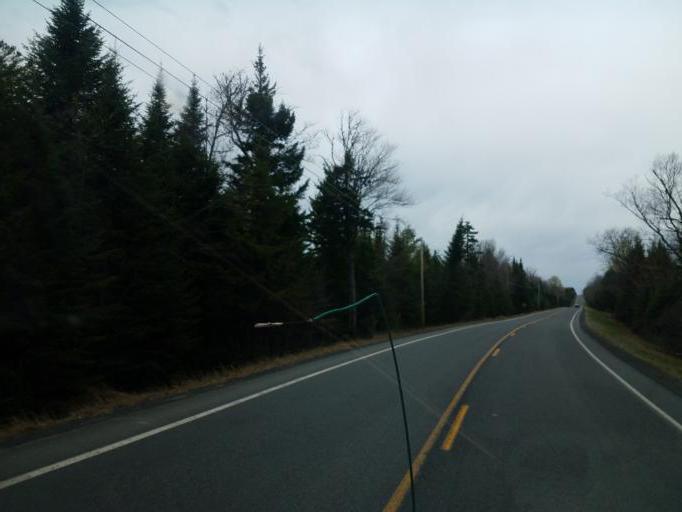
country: US
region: Maine
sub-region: Penobscot County
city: Patten
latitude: 46.2880
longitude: -68.3577
